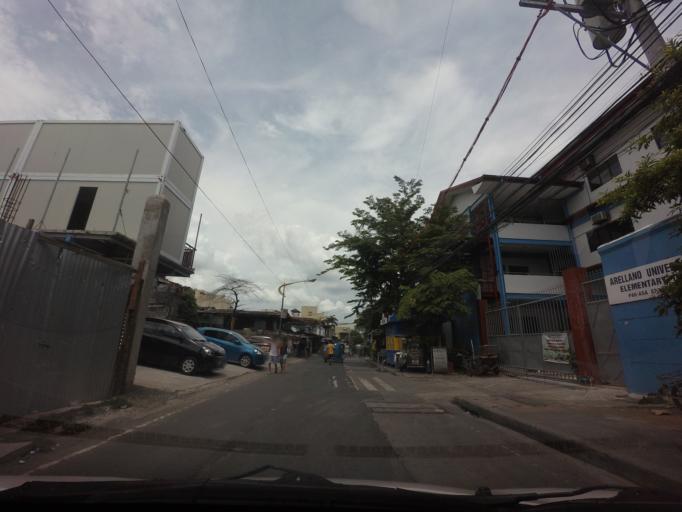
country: PH
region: Metro Manila
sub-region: Pasig
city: Pasig City
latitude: 14.5734
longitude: 121.0801
